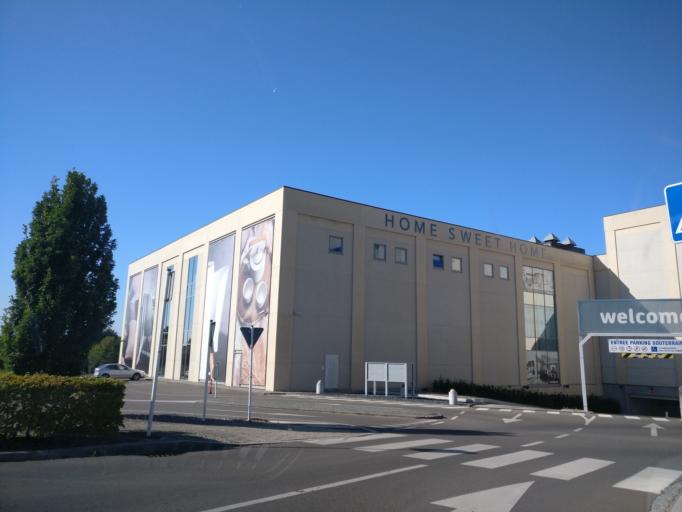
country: LU
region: Luxembourg
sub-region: Canton de Capellen
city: Mamer
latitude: 49.6403
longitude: 6.0138
